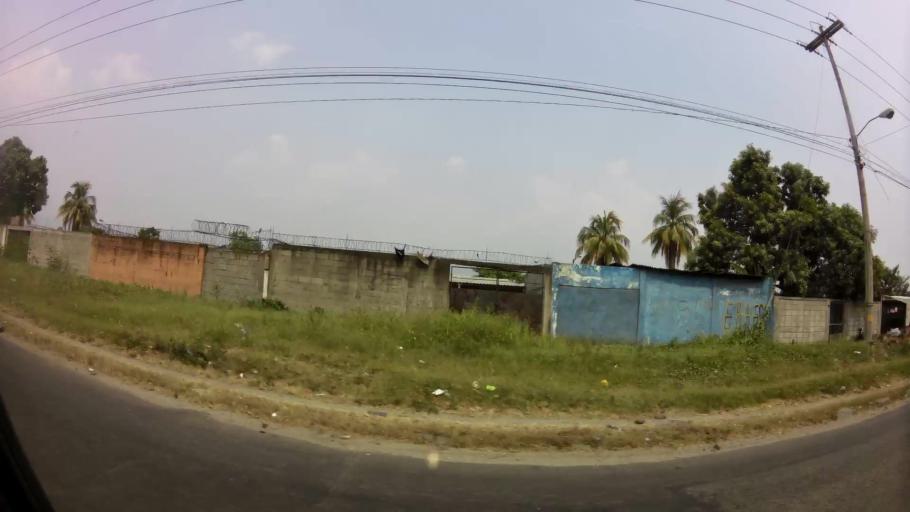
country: HN
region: Cortes
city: San Pedro Sula
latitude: 15.4969
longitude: -88.0052
